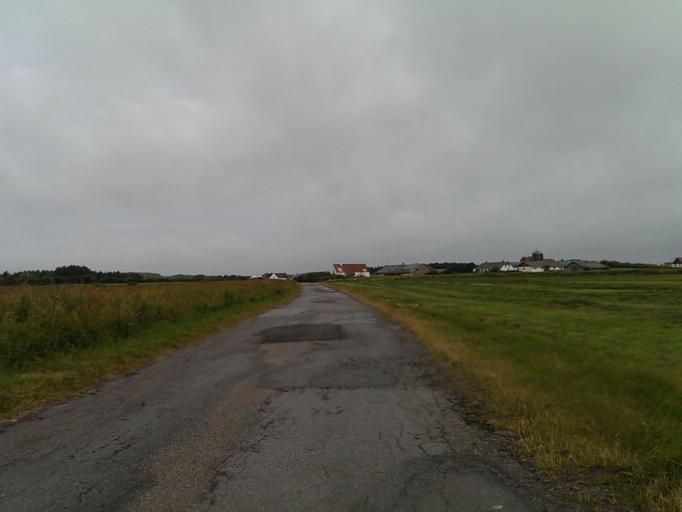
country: DK
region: North Denmark
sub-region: Jammerbugt Kommune
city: Pandrup
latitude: 57.3791
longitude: 9.7358
